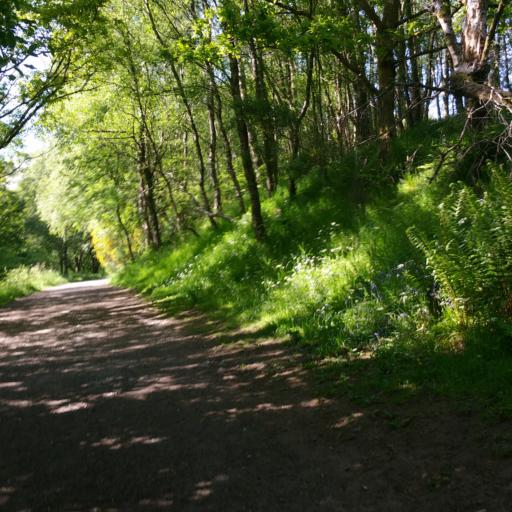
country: GB
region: Scotland
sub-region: East Dunbartonshire
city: Milngavie
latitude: 55.9568
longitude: -4.3305
